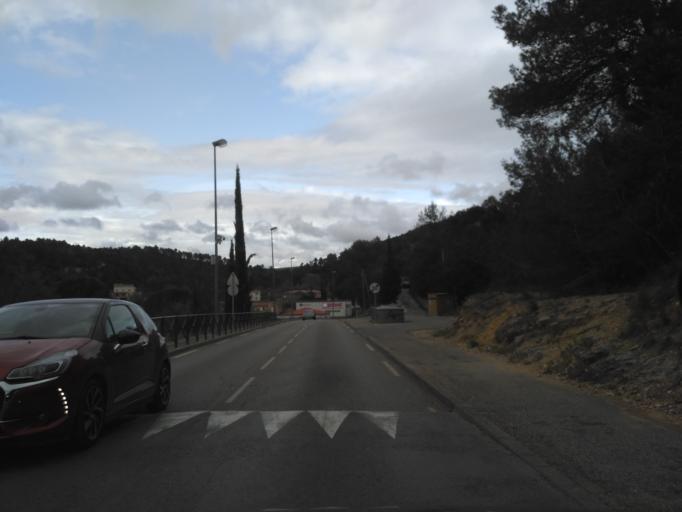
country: FR
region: Provence-Alpes-Cote d'Azur
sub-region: Departement du Var
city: Barjols
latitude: 43.5646
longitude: 6.0096
